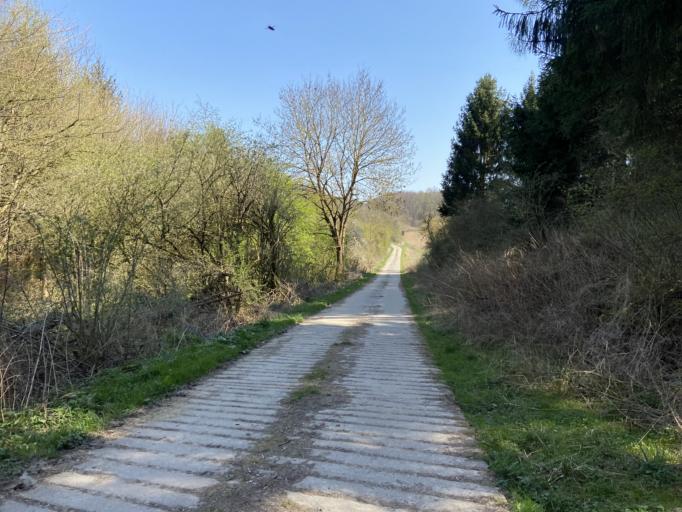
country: DE
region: Lower Saxony
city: Erkerode
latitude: 52.2369
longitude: 10.7271
